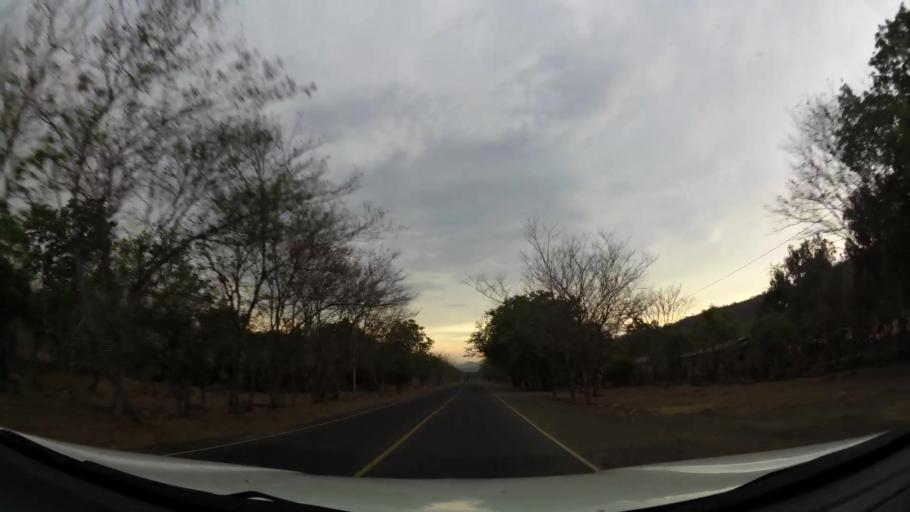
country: NI
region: Leon
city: La Jicaral
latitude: 12.6994
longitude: -86.4021
